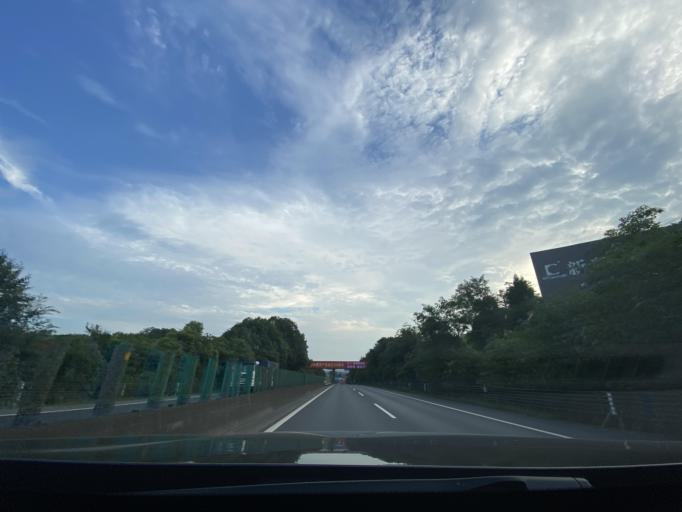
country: CN
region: Sichuan
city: Luojiang
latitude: 31.3927
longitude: 104.5592
